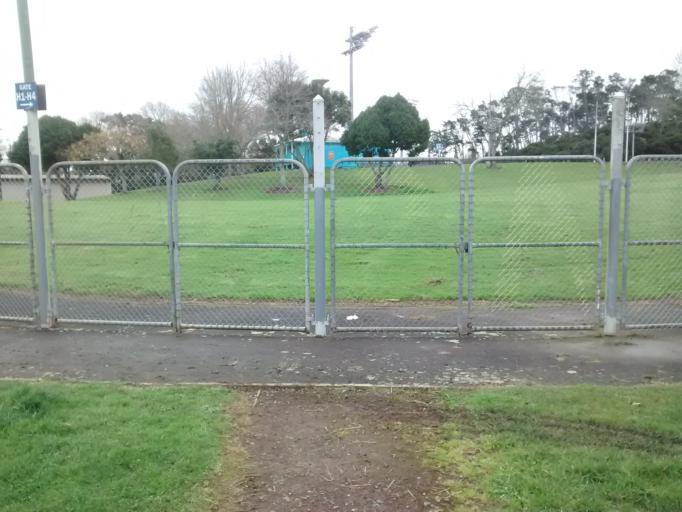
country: NZ
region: Auckland
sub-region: Auckland
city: Auckland
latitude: -36.8651
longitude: 174.7283
